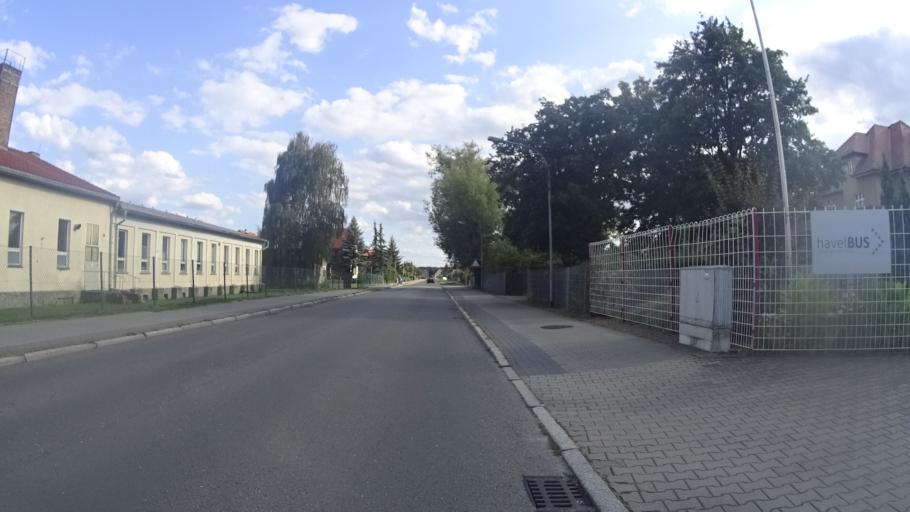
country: DE
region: Brandenburg
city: Rathenow
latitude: 52.5942
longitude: 12.3417
